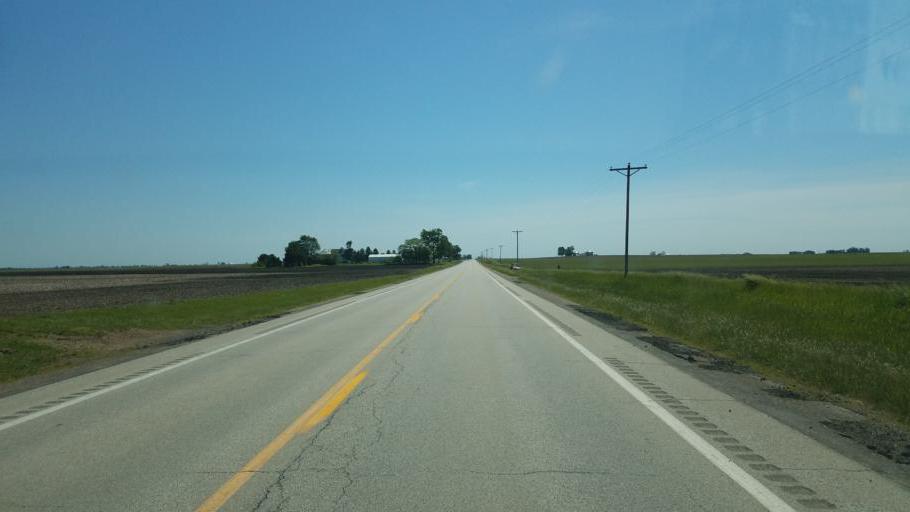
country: US
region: Illinois
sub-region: McLean County
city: Heyworth
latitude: 40.3123
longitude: -88.9074
